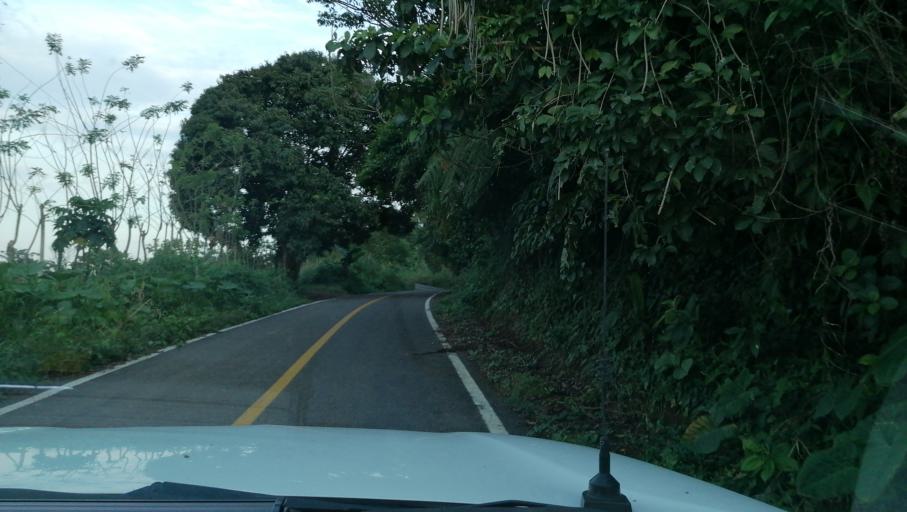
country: MX
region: Chiapas
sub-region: Juarez
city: El Triunfo 1ra. Seccion (Cardona)
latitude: 17.5060
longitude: -93.2265
